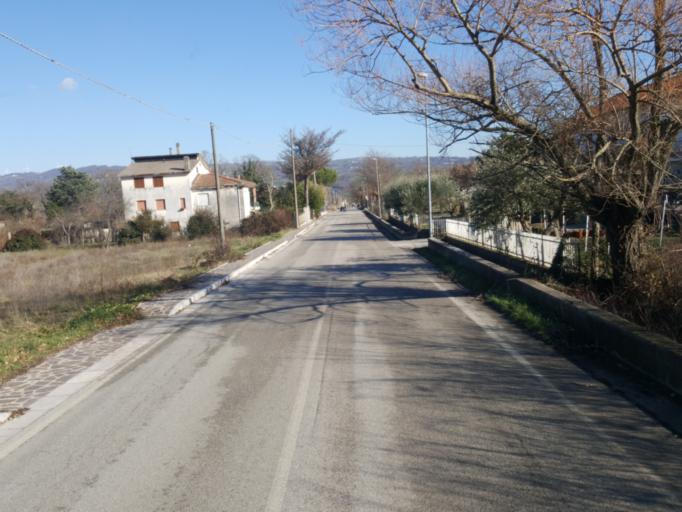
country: IT
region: Campania
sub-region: Provincia di Benevento
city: Morcone
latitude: 41.3433
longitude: 14.6820
